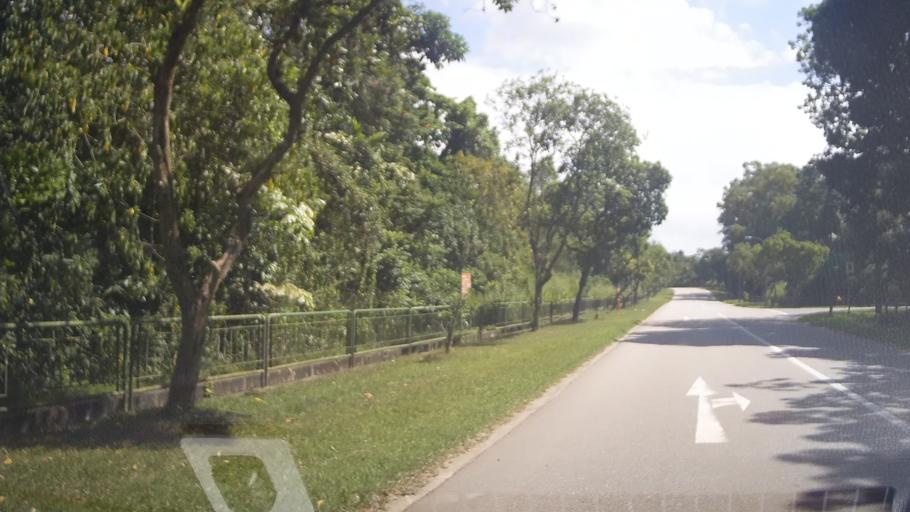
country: MY
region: Johor
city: Johor Bahru
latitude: 1.4280
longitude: 103.7079
